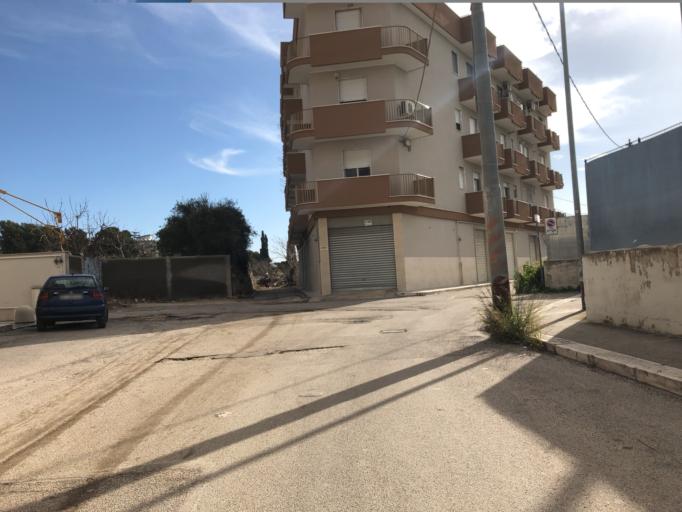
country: IT
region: Apulia
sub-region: Provincia di Barletta - Andria - Trani
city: Andria
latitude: 41.2177
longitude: 16.3052
